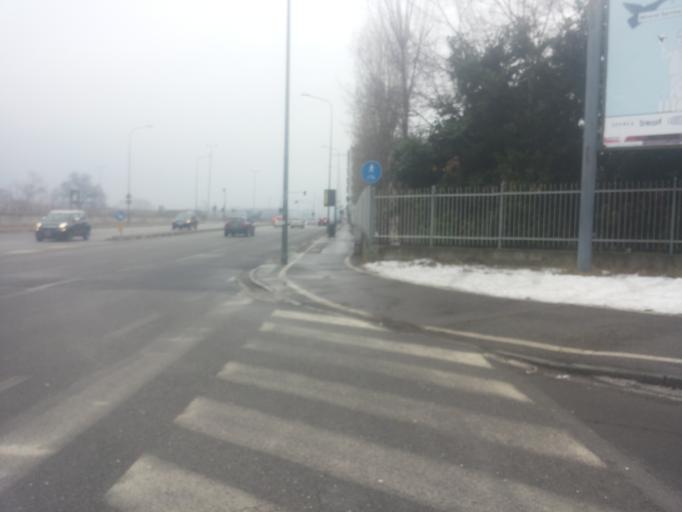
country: IT
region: Piedmont
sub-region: Provincia di Torino
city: Lesna
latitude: 45.0556
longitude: 7.6329
